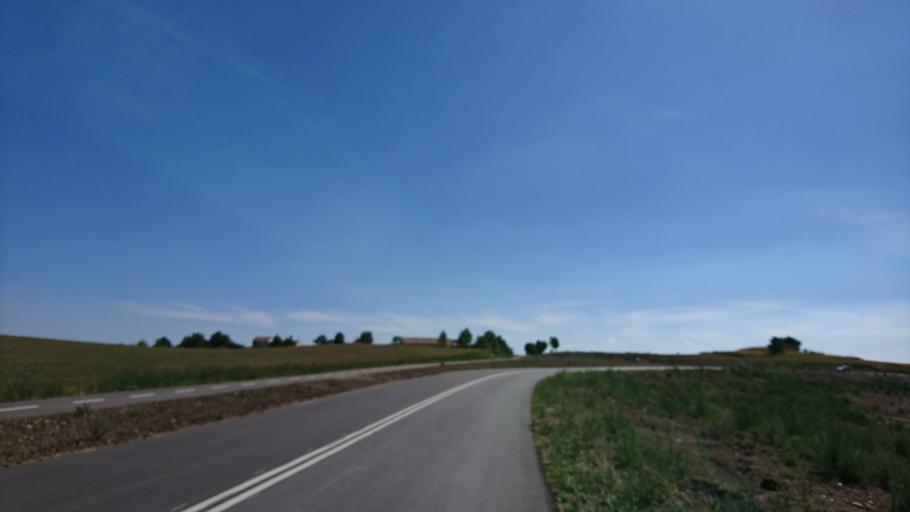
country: DK
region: Capital Region
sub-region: Ballerup Kommune
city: Malov
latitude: 55.7589
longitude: 12.3093
